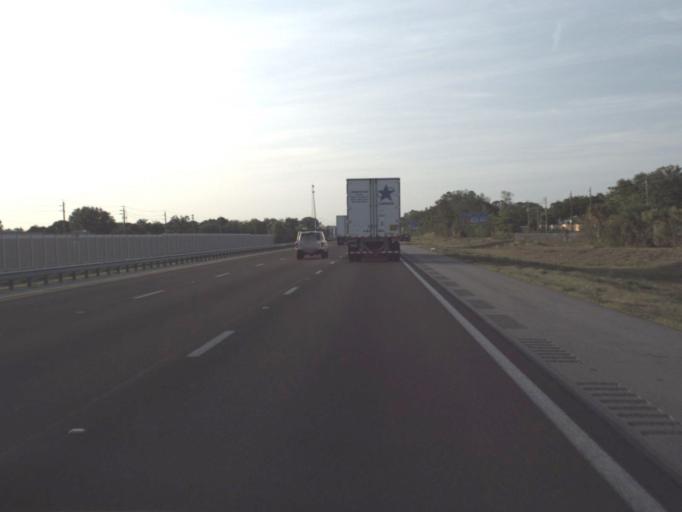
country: US
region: Florida
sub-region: Brevard County
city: Mims
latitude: 28.6534
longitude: -80.8643
